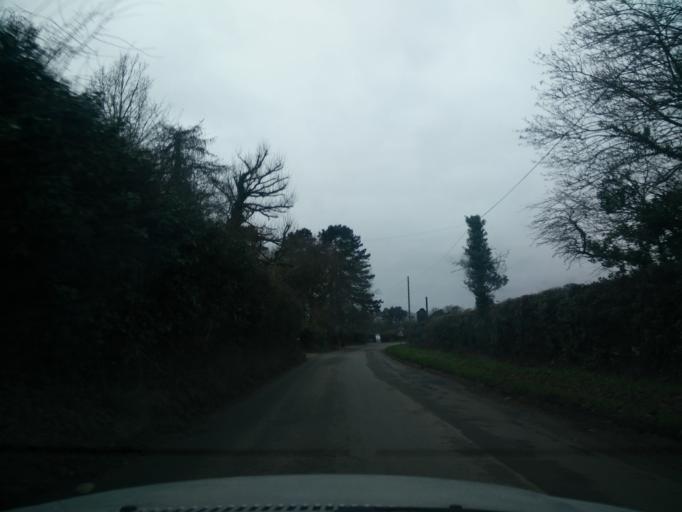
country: GB
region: England
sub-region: Buckinghamshire
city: Little Chalfont
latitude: 51.6527
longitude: -0.5349
